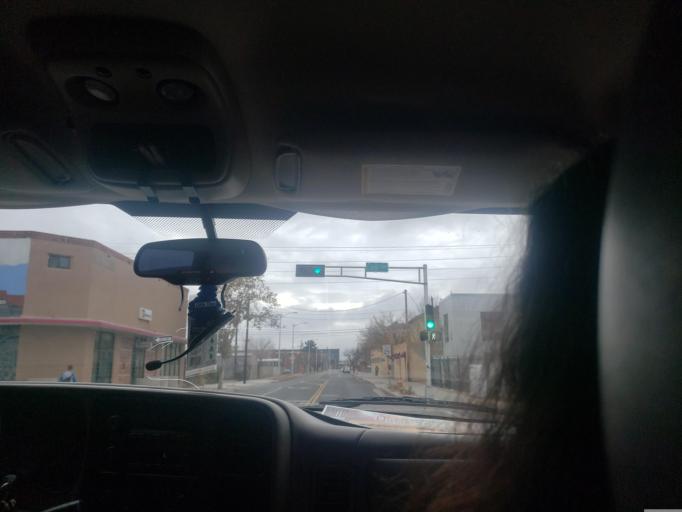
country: US
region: New Mexico
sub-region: Bernalillo County
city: Albuquerque
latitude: 35.0804
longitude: -106.6500
